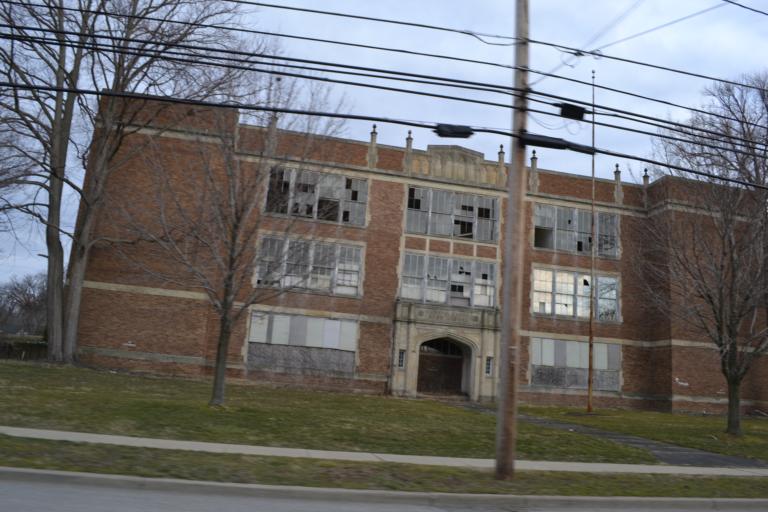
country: US
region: New York
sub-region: Chautauqua County
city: Silver Creek
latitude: 42.5419
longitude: -79.1677
